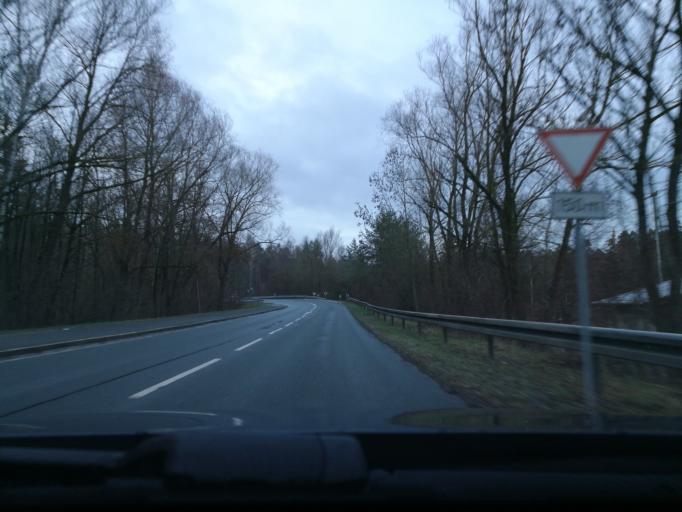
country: DE
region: Bavaria
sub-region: Regierungsbezirk Mittelfranken
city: Heroldsberg
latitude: 49.5215
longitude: 11.1502
